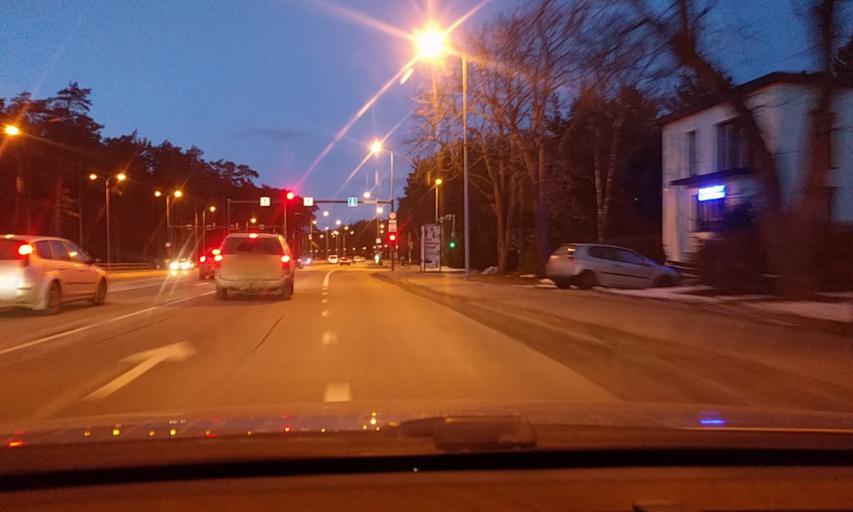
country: EE
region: Harju
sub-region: Viimsi vald
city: Viimsi
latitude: 59.4737
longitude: 24.8372
